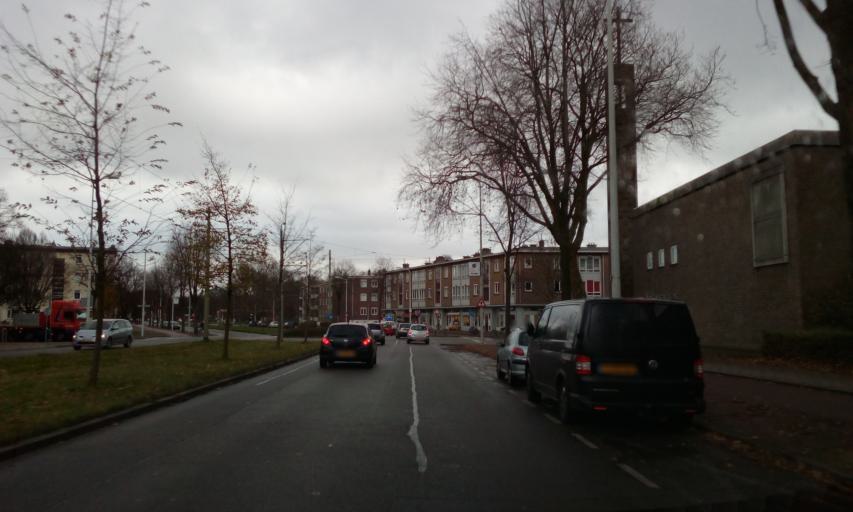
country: NL
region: South Holland
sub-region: Gemeente Den Haag
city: The Hague
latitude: 52.0442
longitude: 4.2905
